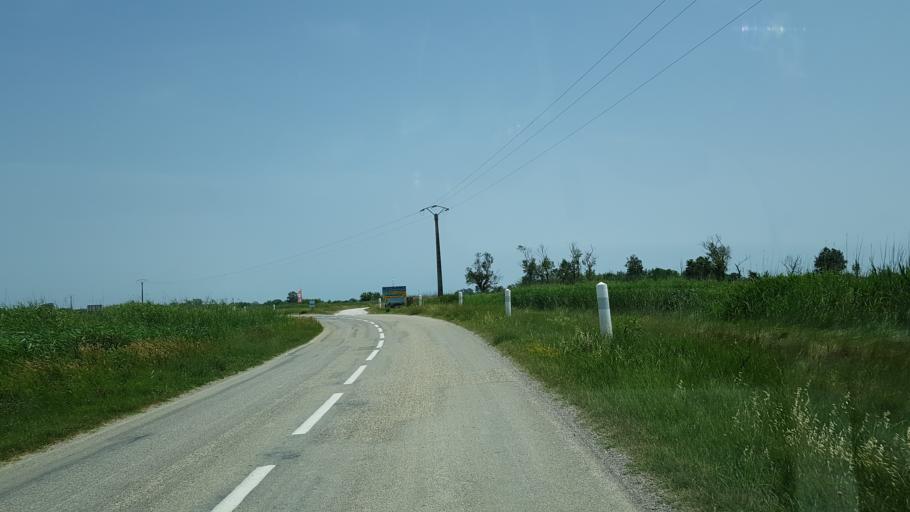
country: FR
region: Provence-Alpes-Cote d'Azur
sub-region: Departement des Bouches-du-Rhone
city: Port-Saint-Louis-du-Rhone
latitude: 43.4447
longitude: 4.6672
